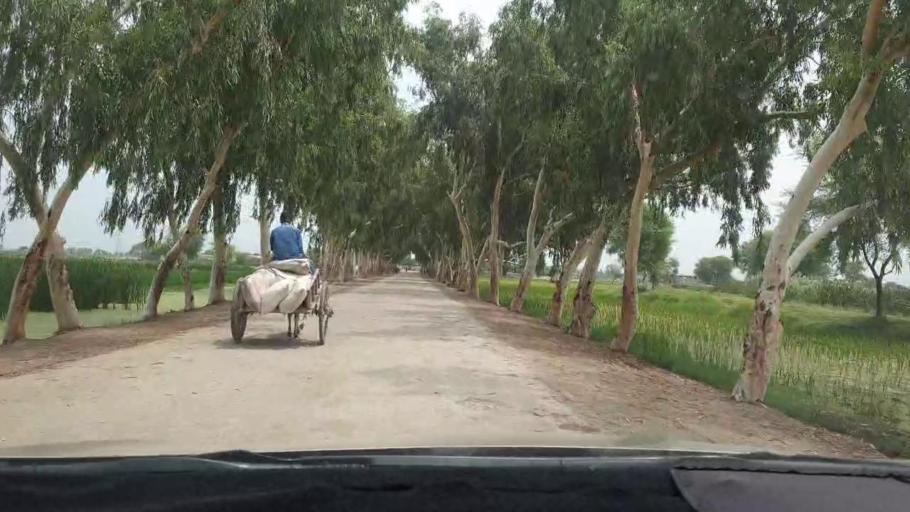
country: PK
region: Sindh
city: Ratodero
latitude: 27.7656
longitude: 68.3261
